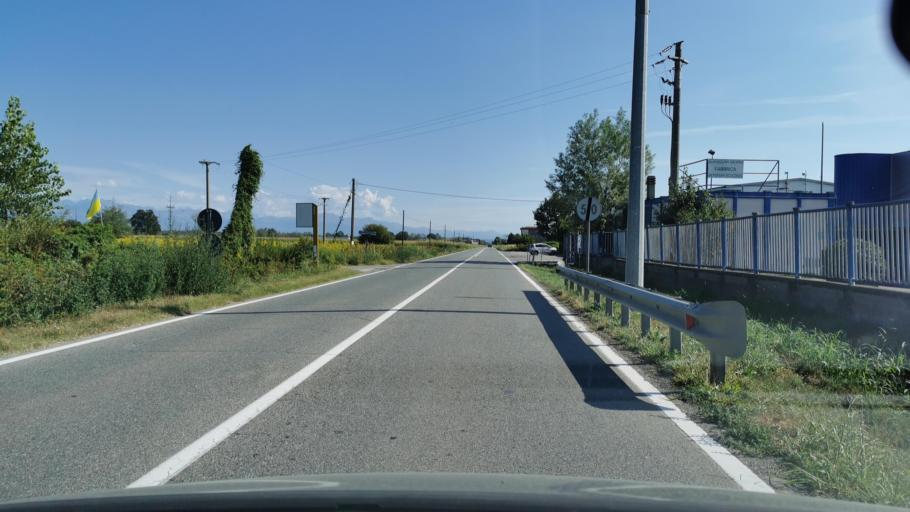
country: IT
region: Piedmont
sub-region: Provincia di Torino
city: Settimo Torinese
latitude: 45.1709
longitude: 7.7614
